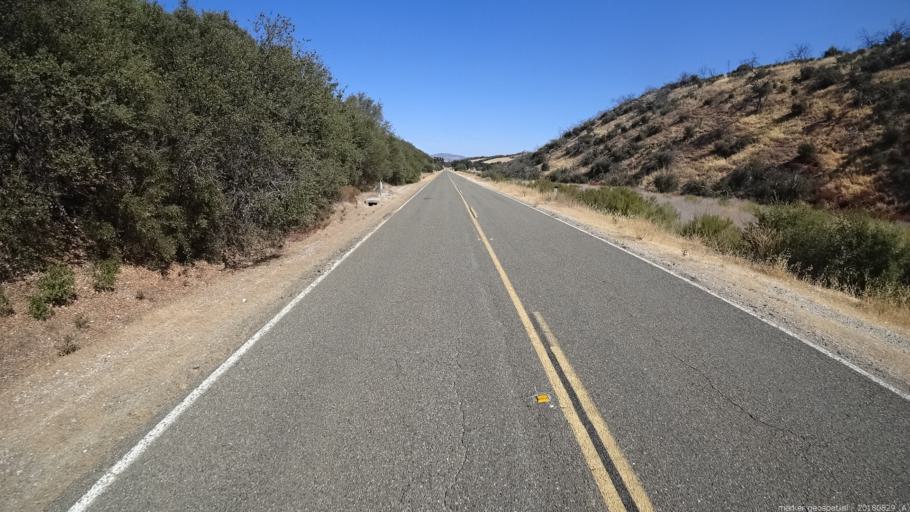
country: US
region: California
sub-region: San Luis Obispo County
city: Lake Nacimiento
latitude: 35.8651
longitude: -121.0623
